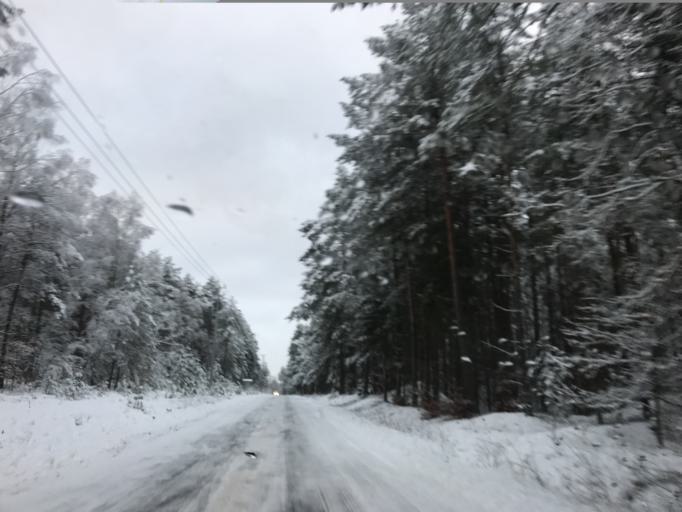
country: PL
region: Pomeranian Voivodeship
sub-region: Powiat bytowski
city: Czarna Dabrowka
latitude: 54.2829
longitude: 17.5962
